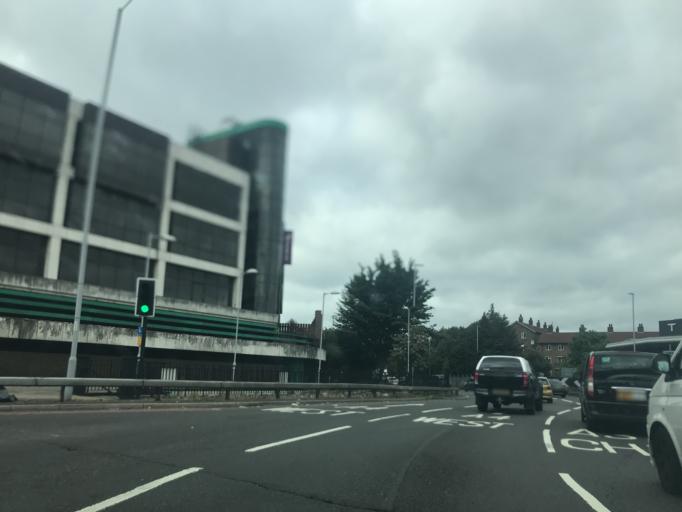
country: GB
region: England
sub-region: Greater London
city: Hammersmith
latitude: 51.4868
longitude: -0.2522
